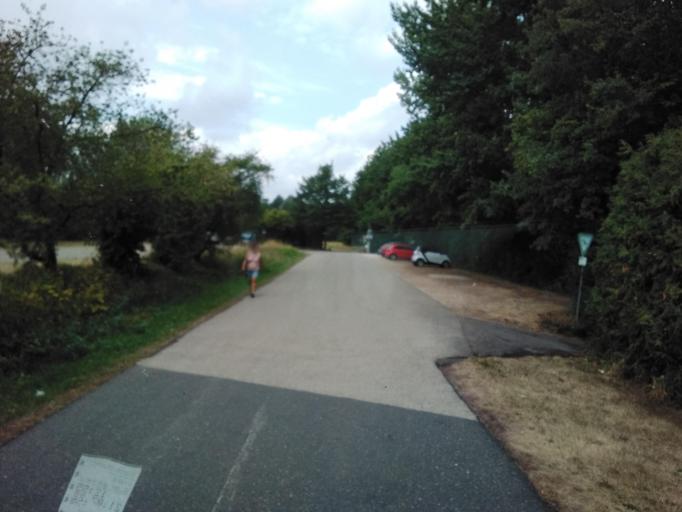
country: DE
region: Bavaria
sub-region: Regierungsbezirk Mittelfranken
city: Allersberg
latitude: 49.2291
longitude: 11.2051
